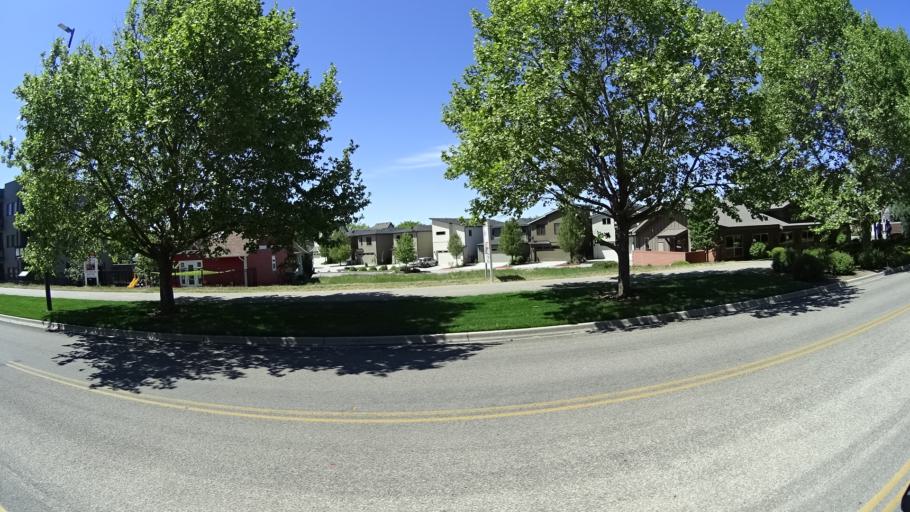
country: US
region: Idaho
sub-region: Ada County
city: Boise
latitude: 43.5683
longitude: -116.1193
